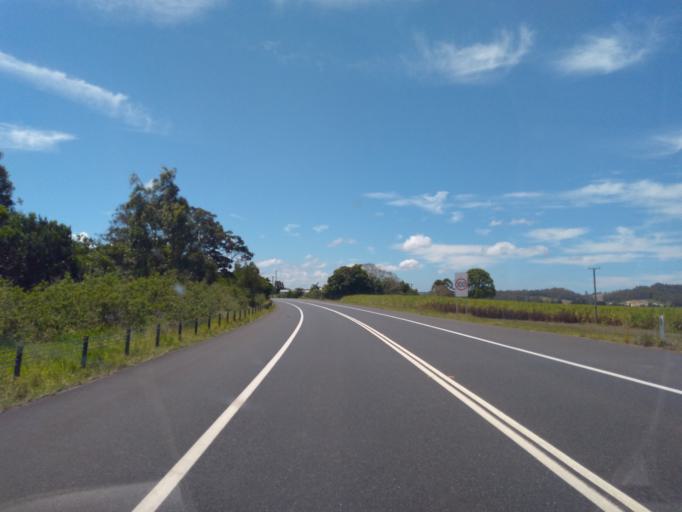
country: AU
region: New South Wales
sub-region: Clarence Valley
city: Maclean
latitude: -29.5319
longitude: 153.1867
